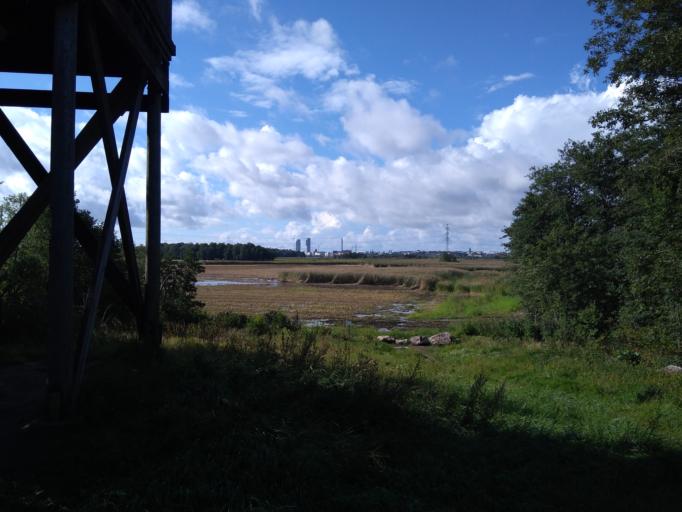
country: FI
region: Uusimaa
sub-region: Helsinki
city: Helsinki
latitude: 60.2190
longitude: 25.0032
